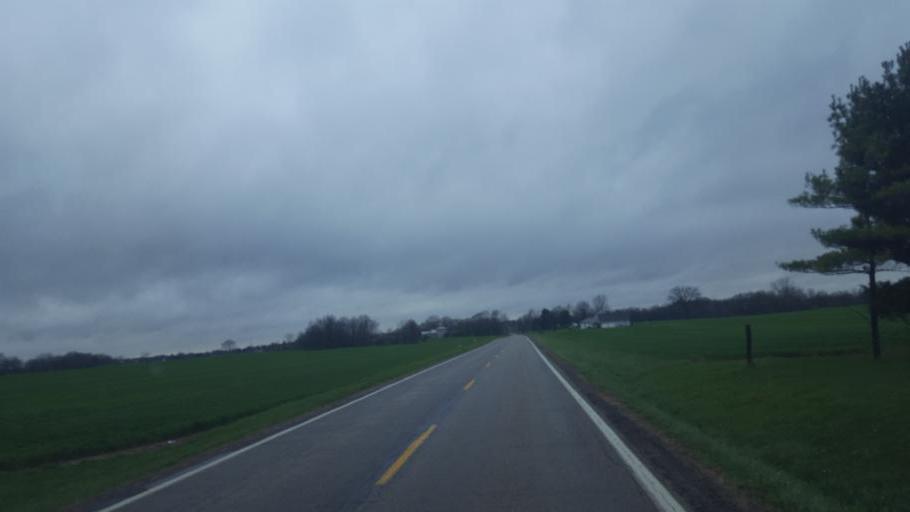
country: US
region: Ohio
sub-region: Morrow County
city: Cardington
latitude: 40.4917
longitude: -82.8689
